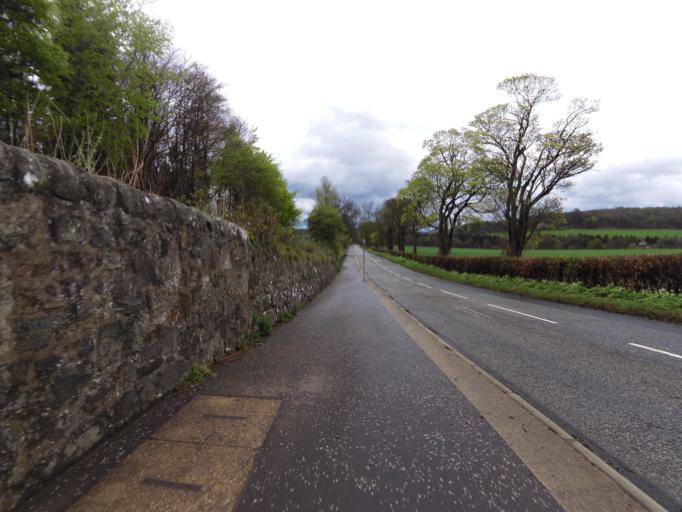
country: GB
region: Scotland
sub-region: Edinburgh
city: Queensferry
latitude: 55.9835
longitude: -3.3559
